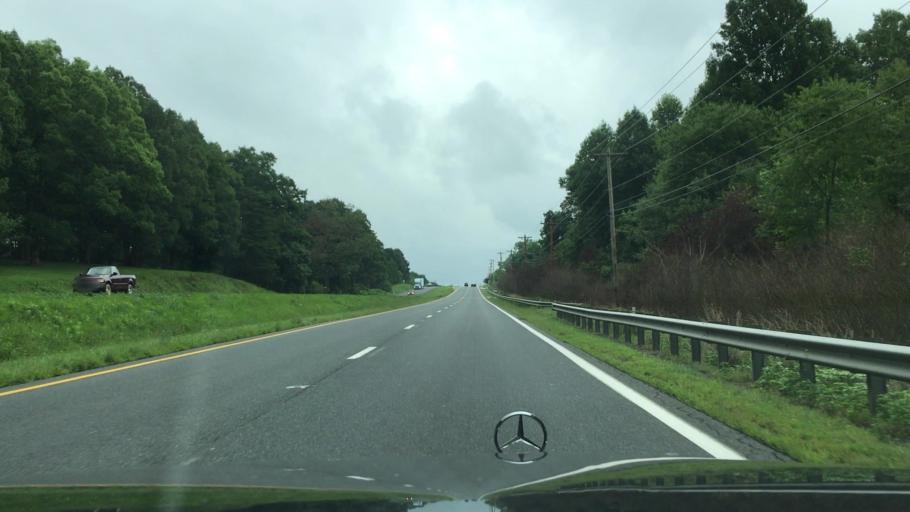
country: US
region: Virginia
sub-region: Campbell County
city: Concord
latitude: 37.3679
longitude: -79.0138
